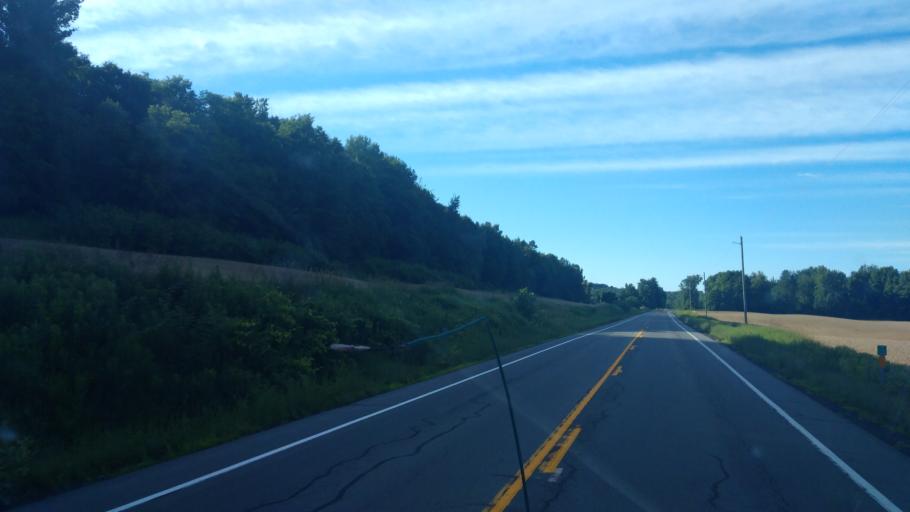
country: US
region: New York
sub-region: Wayne County
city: Lyons
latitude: 43.0995
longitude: -76.9846
